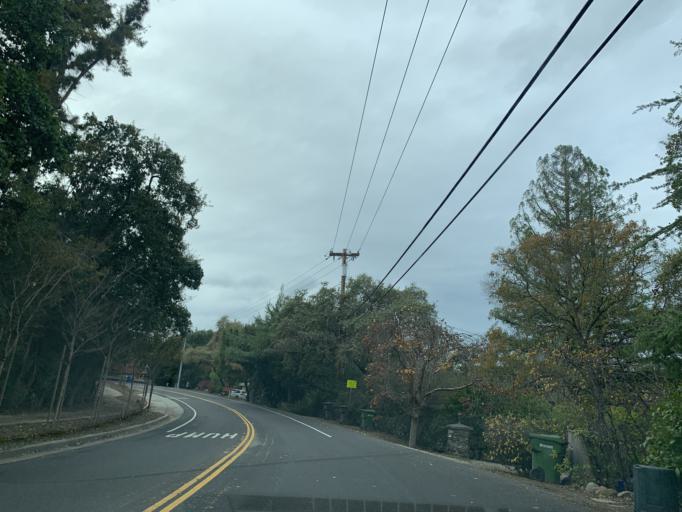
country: US
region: California
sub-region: Santa Clara County
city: Monte Sereno
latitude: 37.2609
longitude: -121.9779
